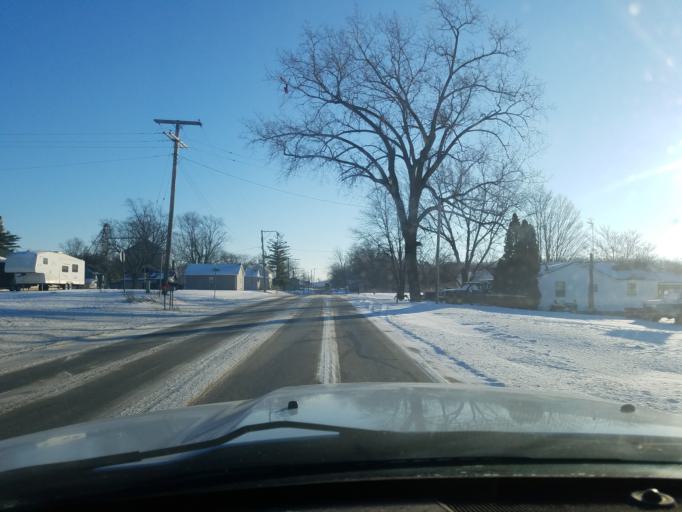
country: US
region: Indiana
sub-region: Noble County
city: Albion
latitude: 41.4569
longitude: -85.4864
